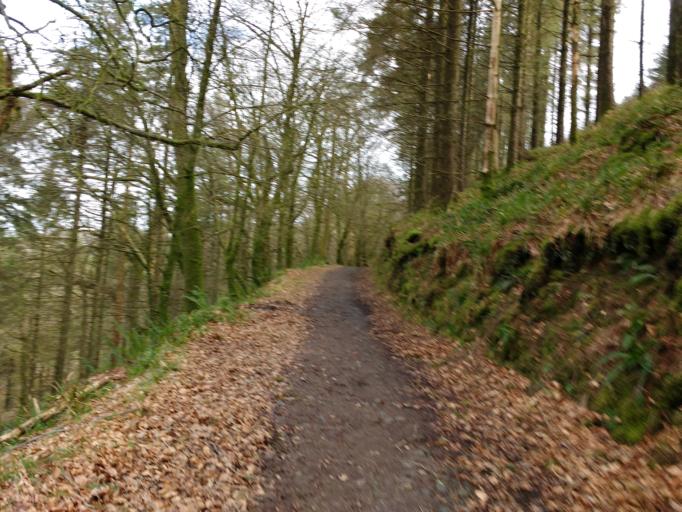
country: IE
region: Leinster
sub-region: Kilkenny
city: Callan
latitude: 52.6608
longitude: -7.5355
